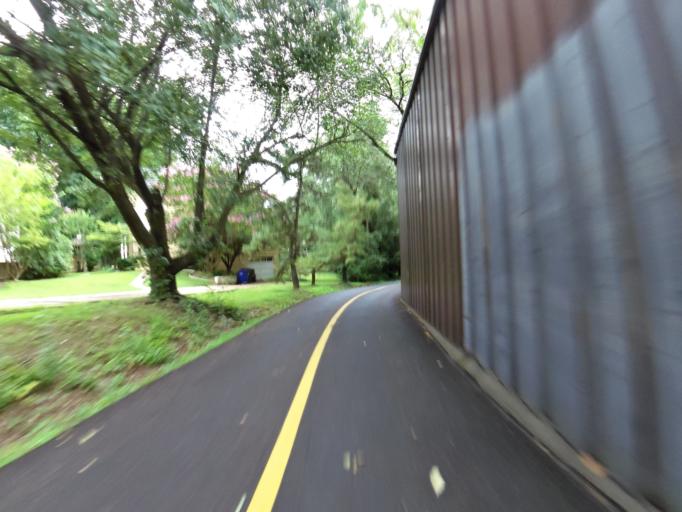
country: US
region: Virginia
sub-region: Arlington County
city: Arlington
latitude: 38.8842
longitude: -77.1201
